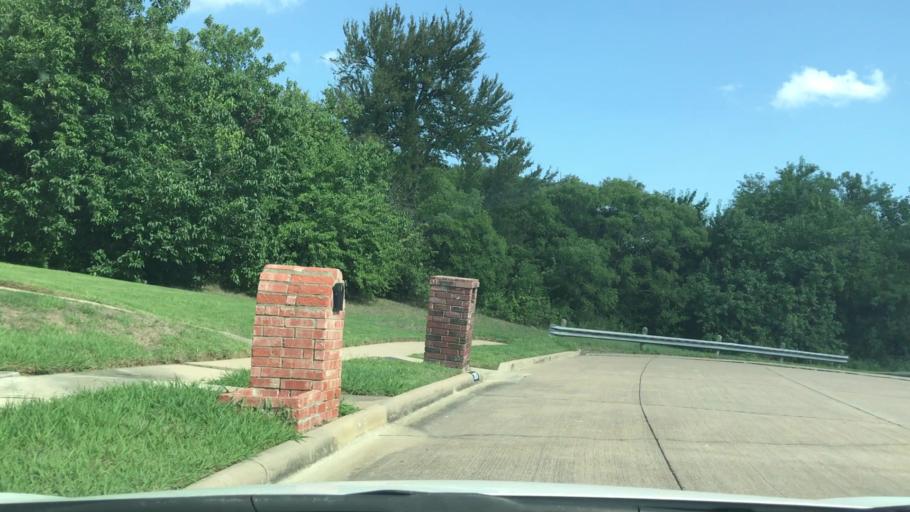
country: US
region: Texas
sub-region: Dallas County
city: Addison
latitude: 32.9733
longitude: -96.8602
